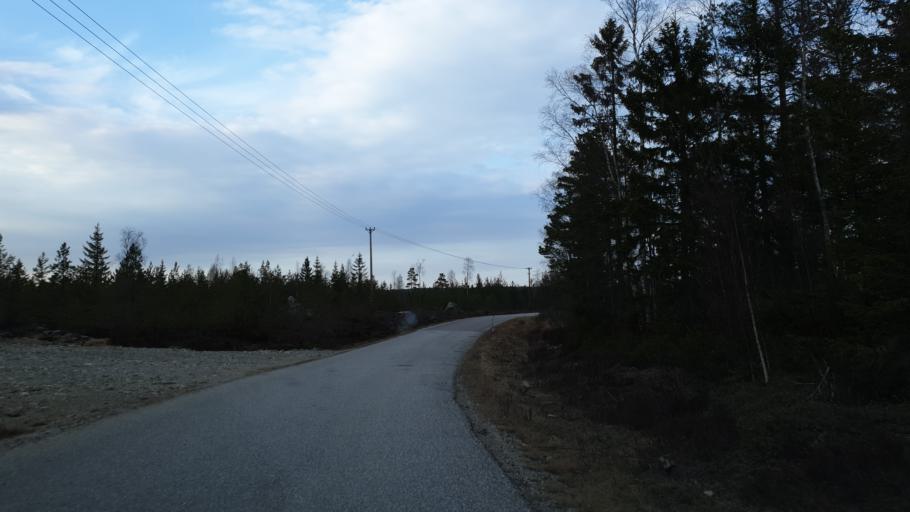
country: SE
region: Vaesternorrland
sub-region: Sundsvalls Kommun
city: Njurundabommen
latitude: 62.0152
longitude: 17.4012
